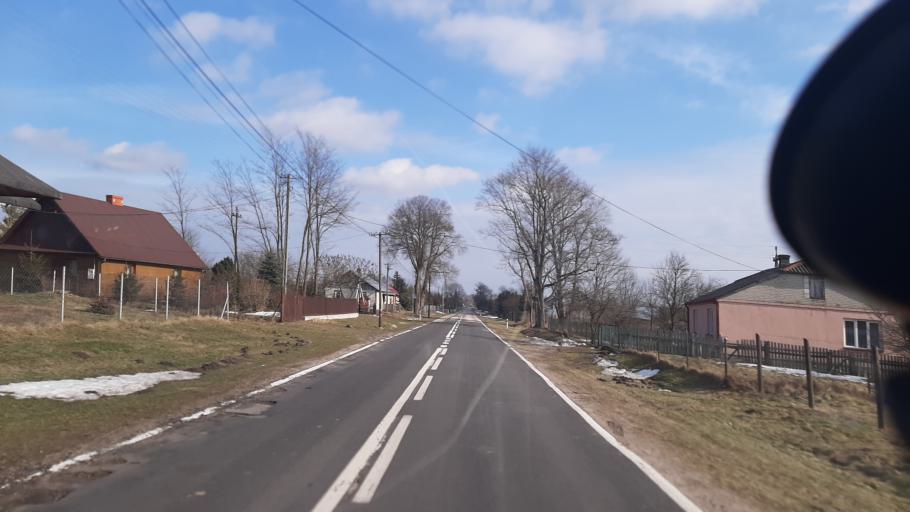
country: PL
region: Lublin Voivodeship
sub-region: Powiat wlodawski
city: Urszulin
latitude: 51.4938
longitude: 23.2254
